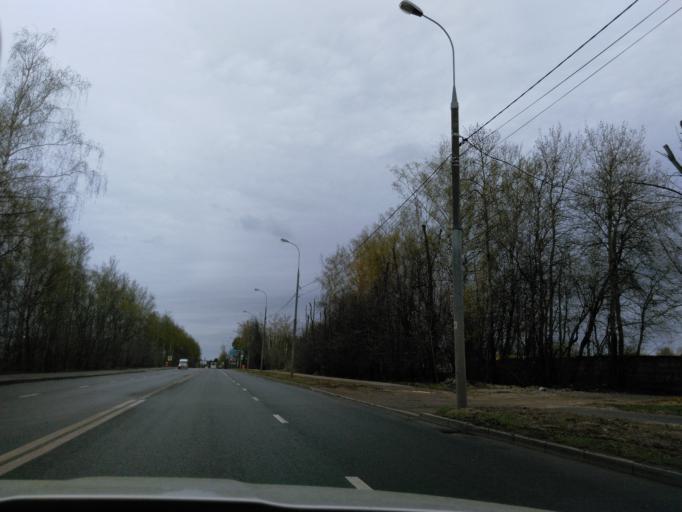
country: RU
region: Moskovskaya
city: Novopodrezkovo
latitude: 55.9096
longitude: 37.3732
